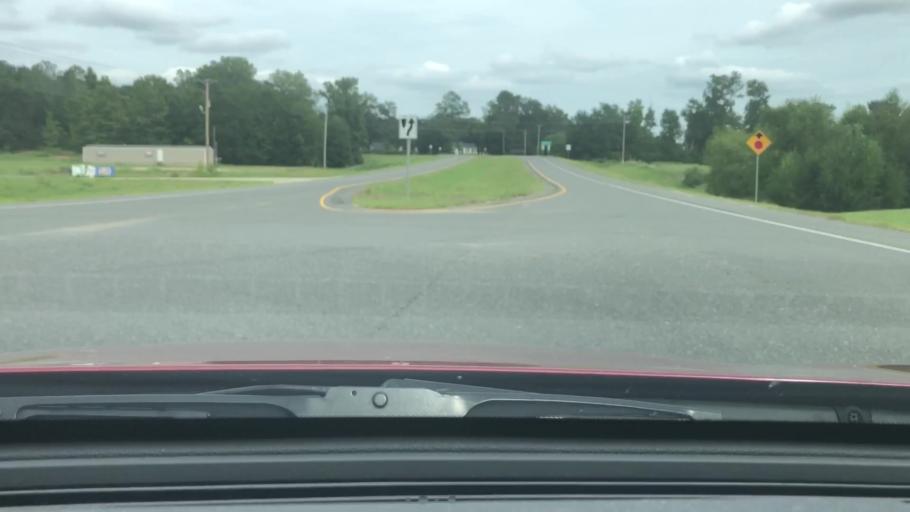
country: US
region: Louisiana
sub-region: Caddo Parish
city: Vivian
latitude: 32.9437
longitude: -93.8945
